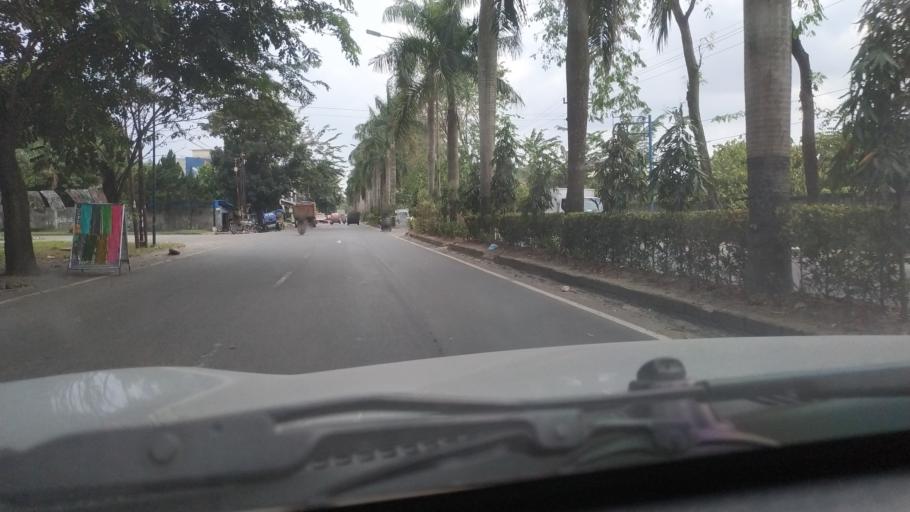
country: ID
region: North Sumatra
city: Sunggal
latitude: 3.5880
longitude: 98.6118
